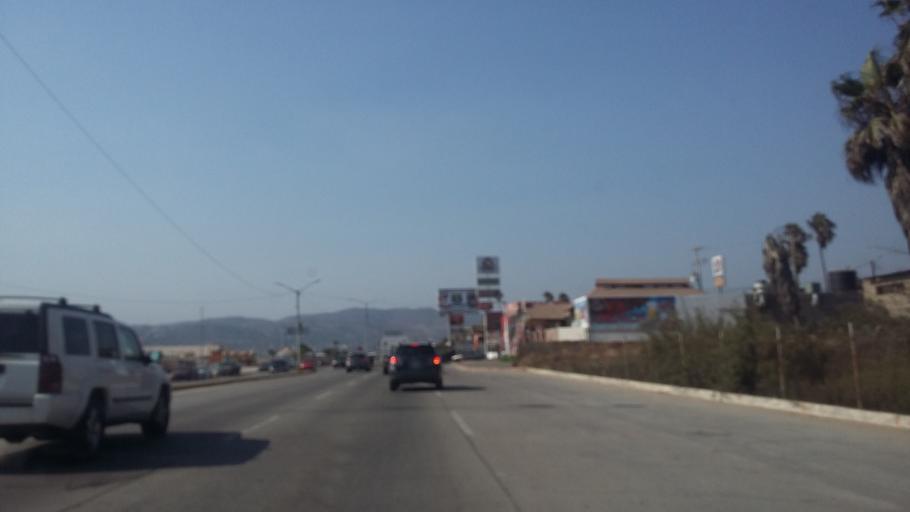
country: MX
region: Baja California
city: Ensenada
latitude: 31.8397
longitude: -116.6107
